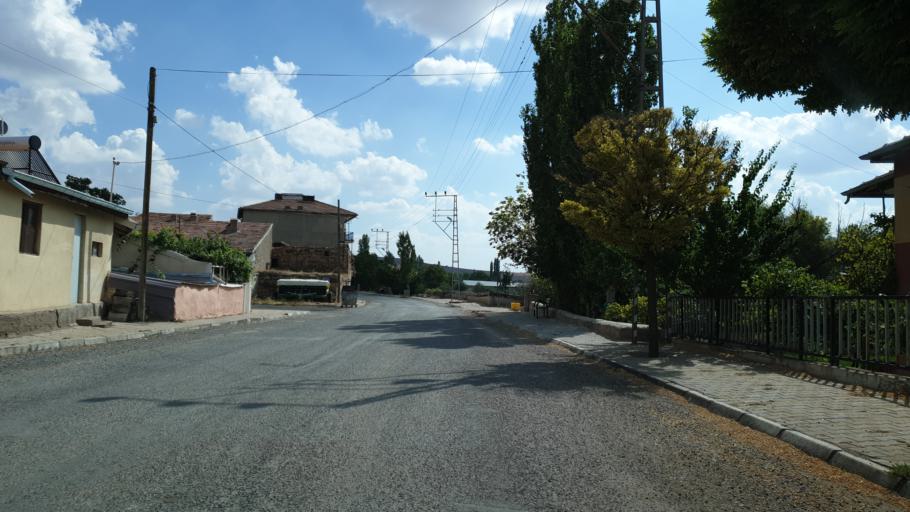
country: TR
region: Kayseri
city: Felahiye
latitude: 39.0934
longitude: 35.5632
